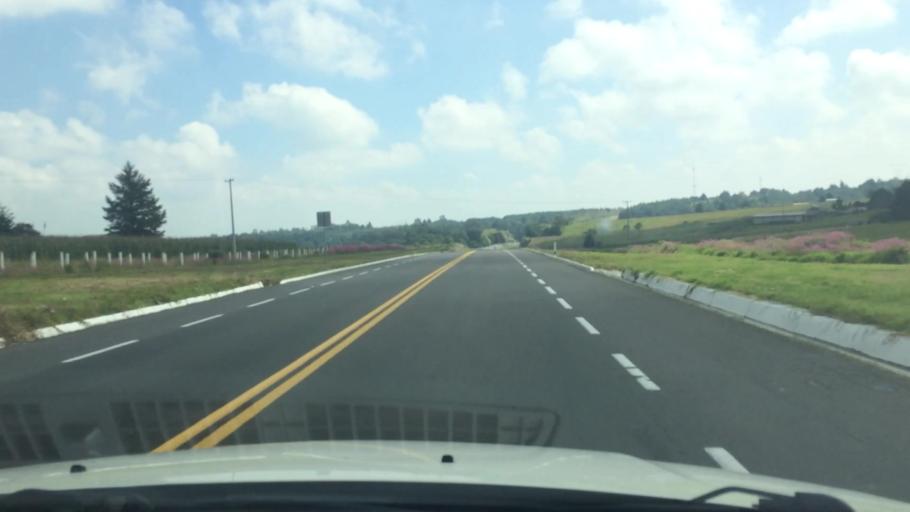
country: MX
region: Mexico
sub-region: Villa Victoria
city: Colonia Doctor Gustavo Baz
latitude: 19.3738
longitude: -99.9128
